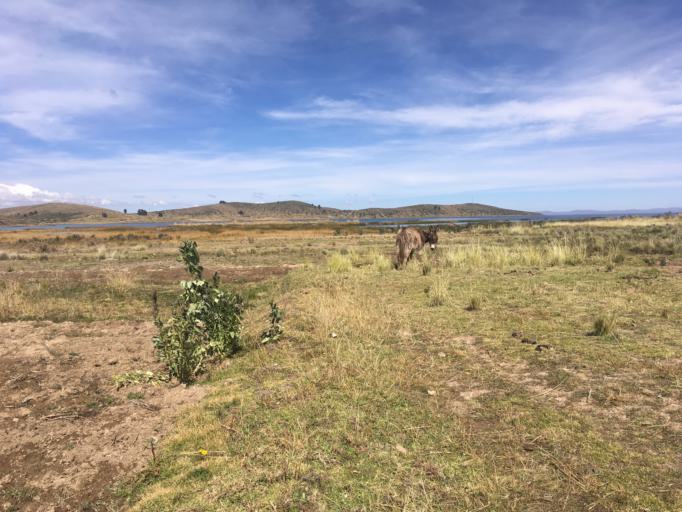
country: BO
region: La Paz
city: San Pedro
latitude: -16.2627
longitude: -68.8746
